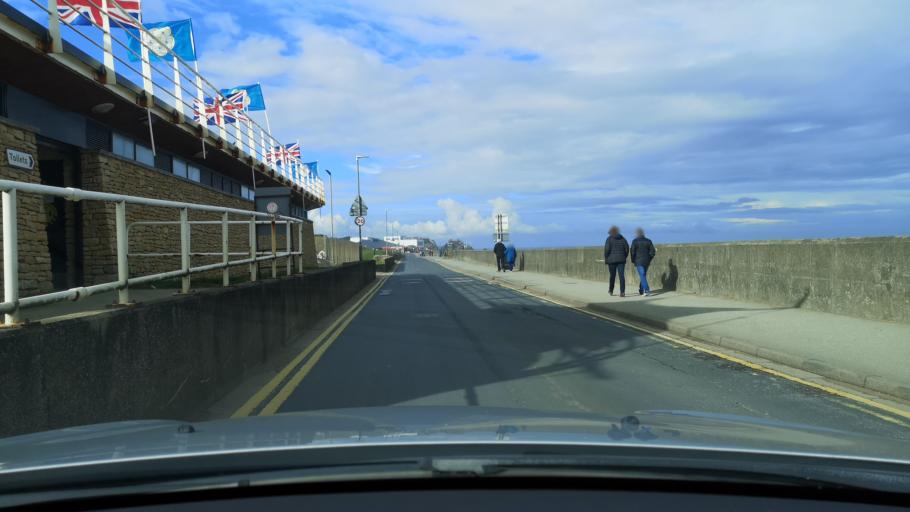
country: GB
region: England
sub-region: East Riding of Yorkshire
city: Hornsea
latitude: 53.9085
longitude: -0.1582
